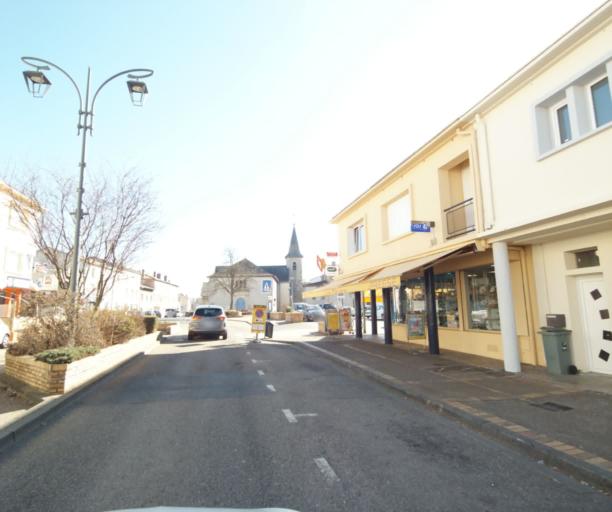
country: FR
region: Lorraine
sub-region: Departement de Meurthe-et-Moselle
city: Tomblaine
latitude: 48.6869
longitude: 6.2103
